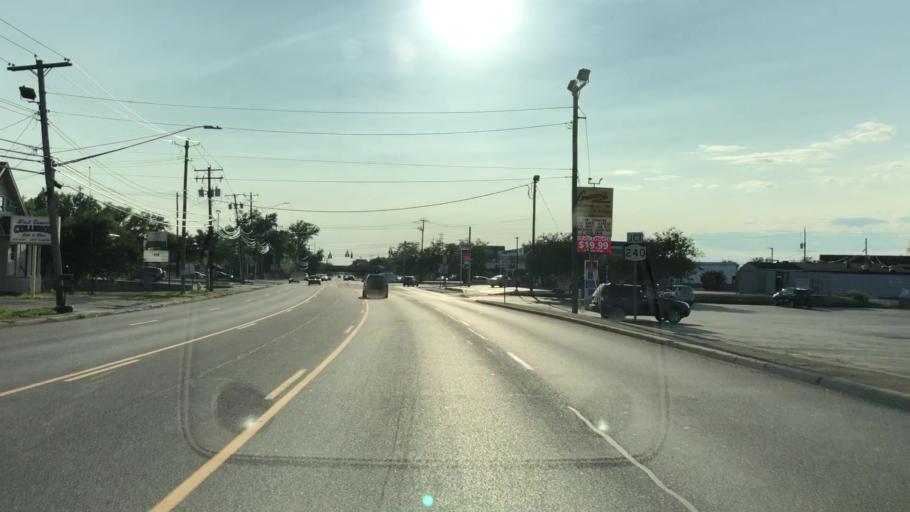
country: US
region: New York
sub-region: Erie County
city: Sloan
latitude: 42.8715
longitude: -78.7854
